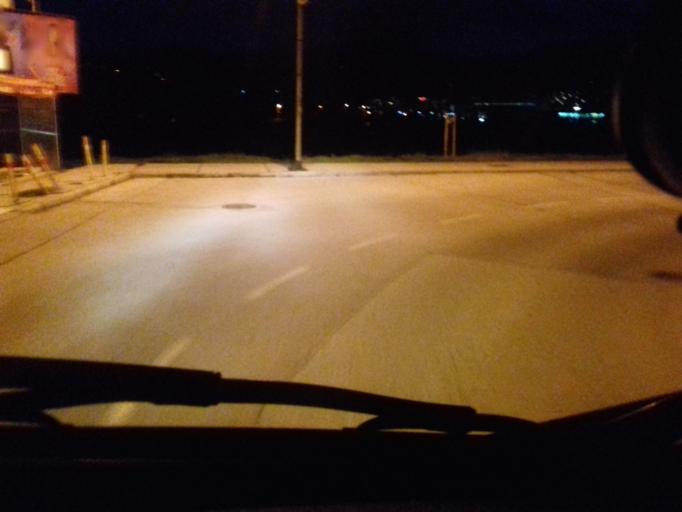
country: BA
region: Federation of Bosnia and Herzegovina
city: Zenica
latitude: 44.2083
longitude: 17.9144
